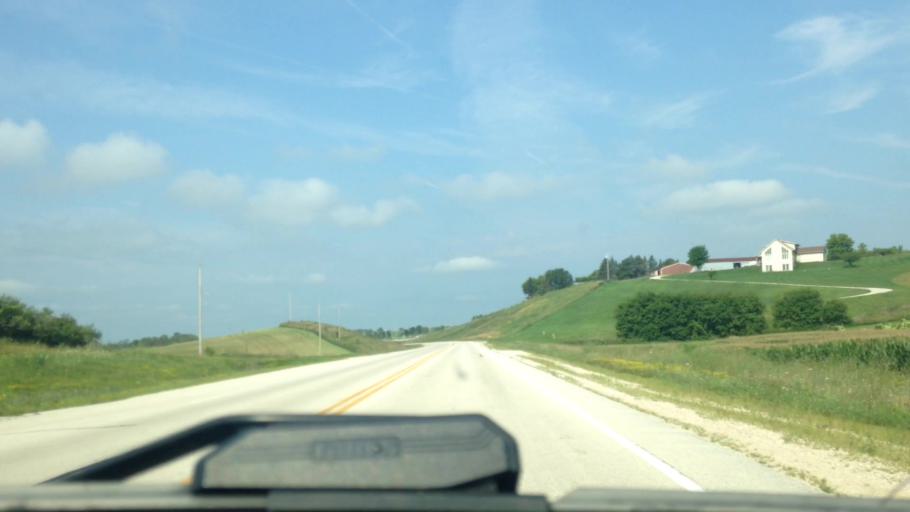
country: US
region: Wisconsin
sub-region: Dodge County
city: Theresa
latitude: 43.5368
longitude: -88.4361
